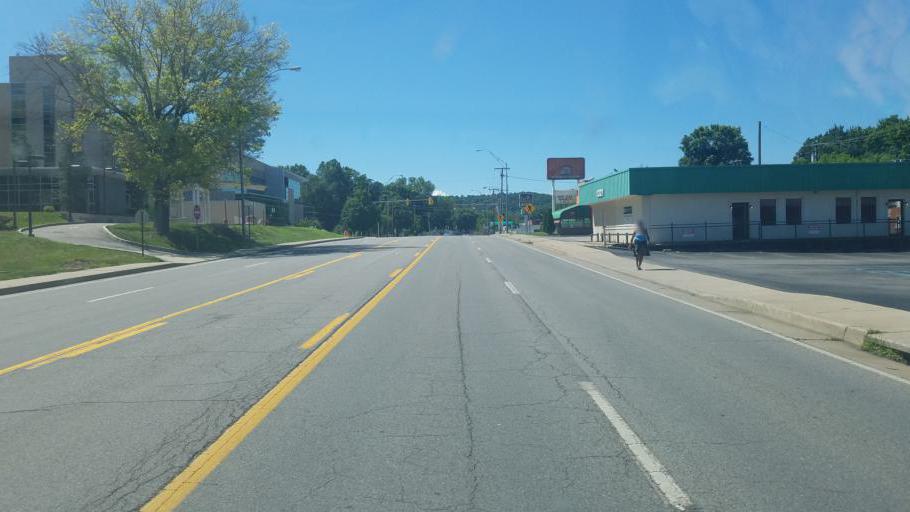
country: US
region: West Virginia
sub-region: Cabell County
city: Huntington
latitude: 38.4102
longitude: -82.4285
